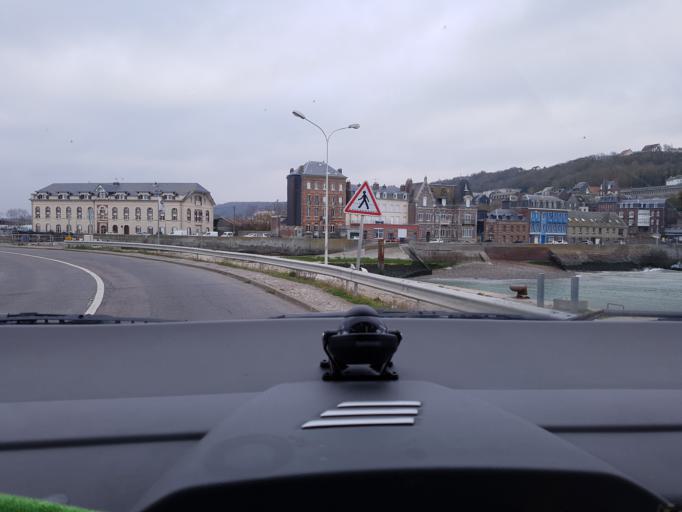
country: FR
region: Haute-Normandie
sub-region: Departement de la Seine-Maritime
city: Le Treport
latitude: 50.0623
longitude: 1.3749
